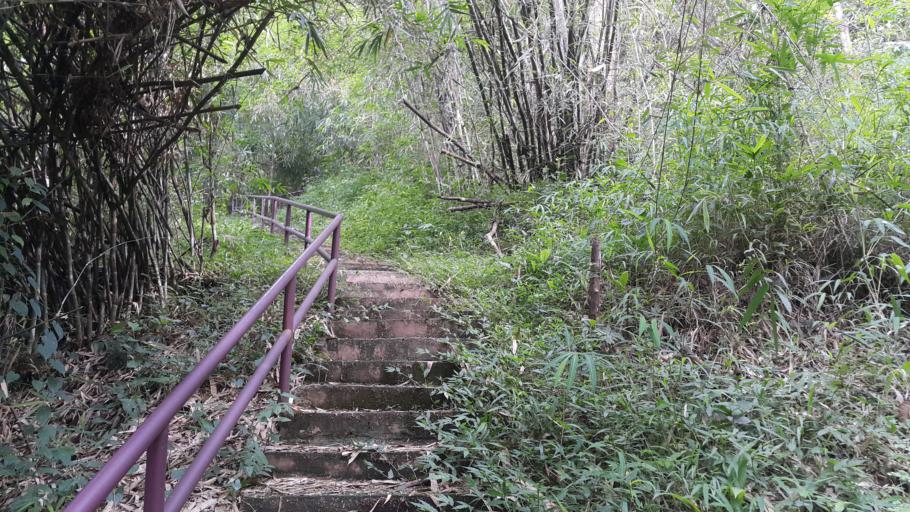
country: TH
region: Loei
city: Na Haeo
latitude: 17.5659
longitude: 100.9923
